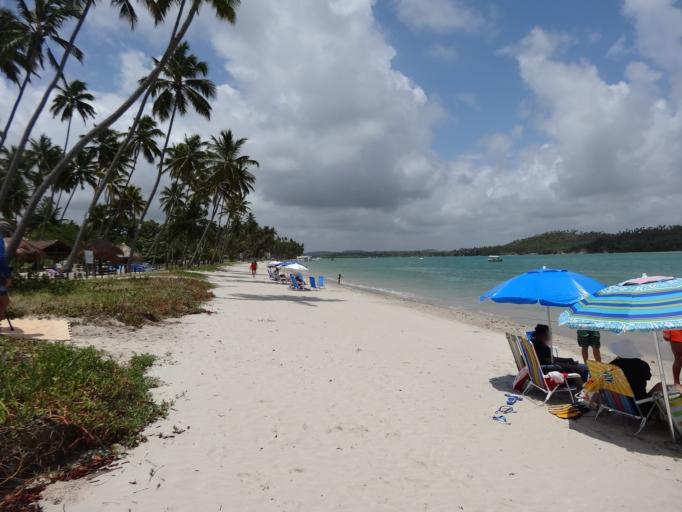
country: BR
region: Pernambuco
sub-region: Tamandare
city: Tamandare
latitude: -8.6976
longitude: -35.0876
